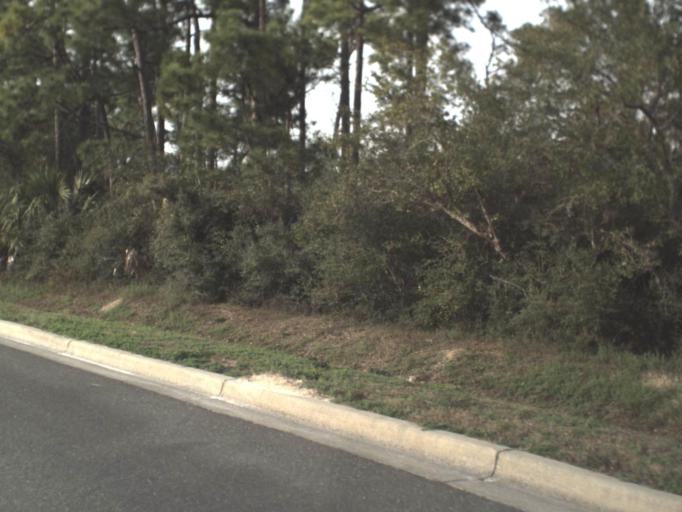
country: US
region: Florida
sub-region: Bay County
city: Mexico Beach
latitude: 29.9539
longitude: -85.4278
